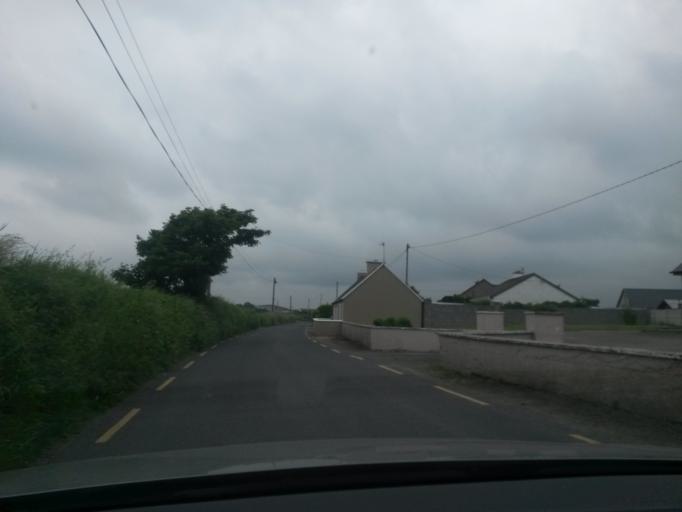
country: IE
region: Munster
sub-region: Ciarrai
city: Tralee
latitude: 52.3691
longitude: -9.7235
